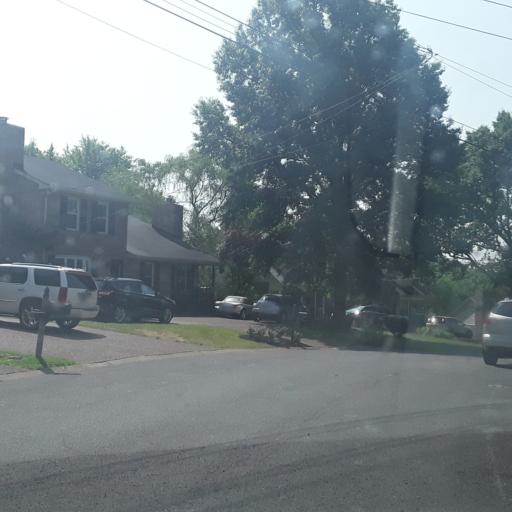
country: US
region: Tennessee
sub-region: Williamson County
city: Brentwood
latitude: 36.0459
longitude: -86.7474
